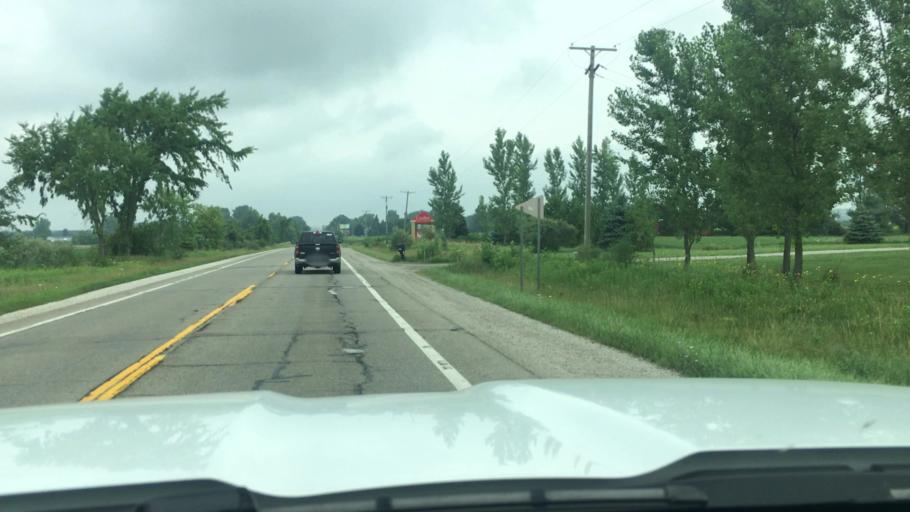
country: US
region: Michigan
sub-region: Sanilac County
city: Brown City
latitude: 43.2019
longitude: -83.0770
